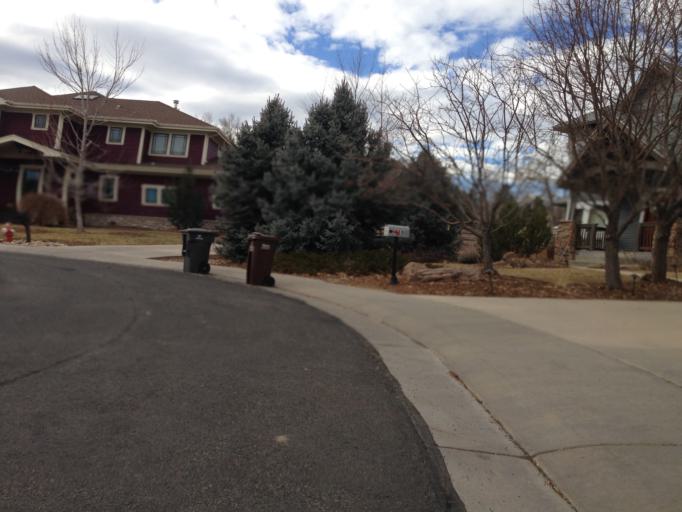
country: US
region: Colorado
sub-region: Boulder County
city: Louisville
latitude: 39.9793
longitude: -105.1457
